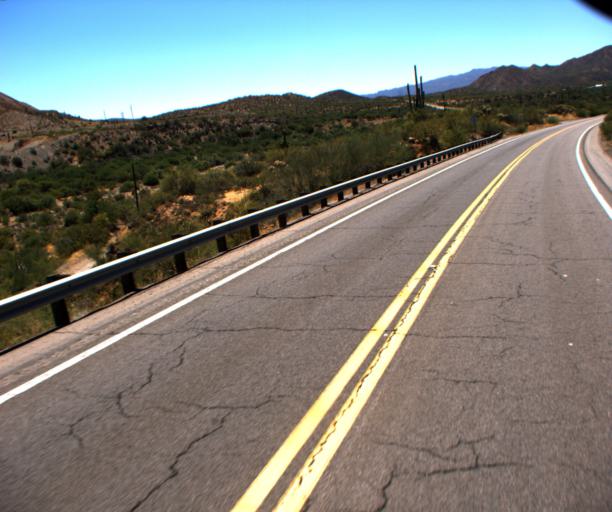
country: US
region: Arizona
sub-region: Pinal County
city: Kearny
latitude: 33.1273
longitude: -110.9788
